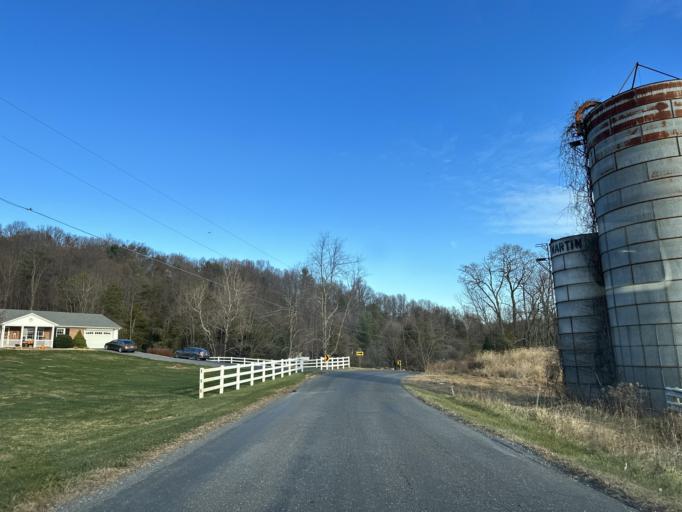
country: US
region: Virginia
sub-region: City of Staunton
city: Staunton
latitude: 38.2403
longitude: -79.2067
